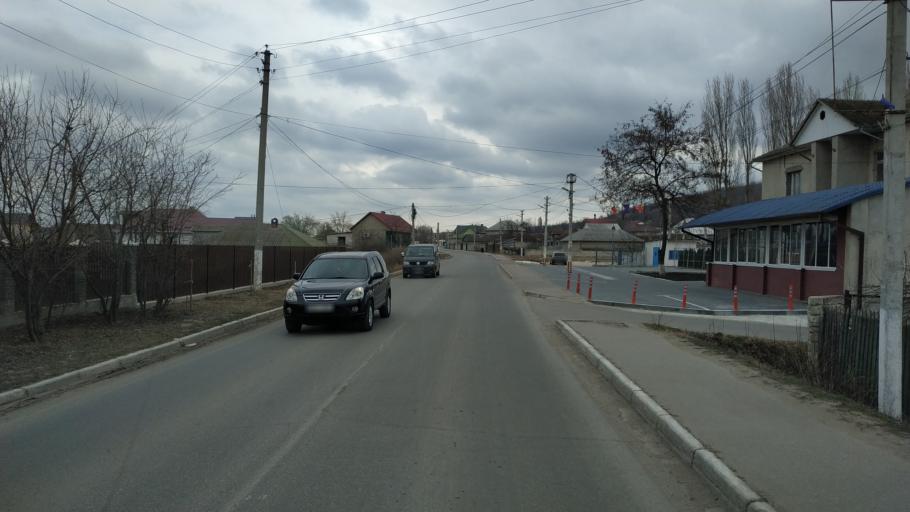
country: MD
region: Laloveni
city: Ialoveni
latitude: 46.8709
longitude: 28.7644
